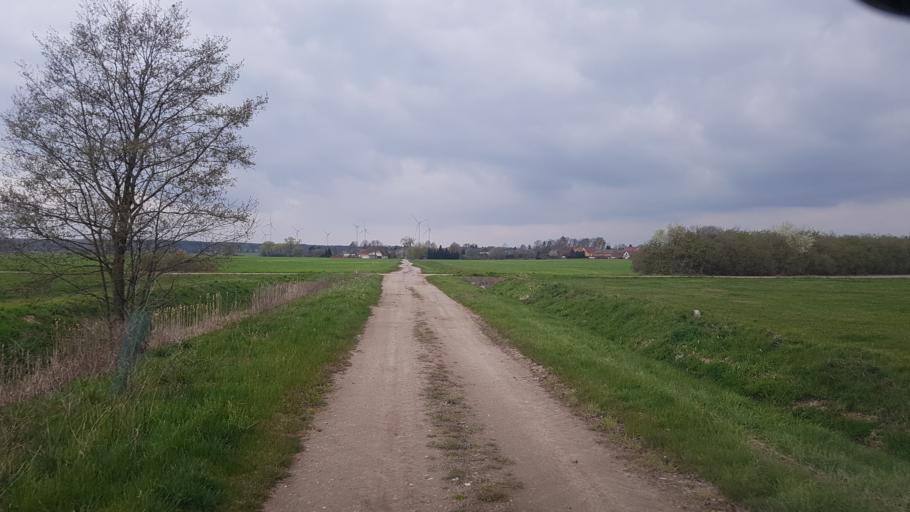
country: DE
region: Brandenburg
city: Sallgast
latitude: 51.6368
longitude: 13.8697
